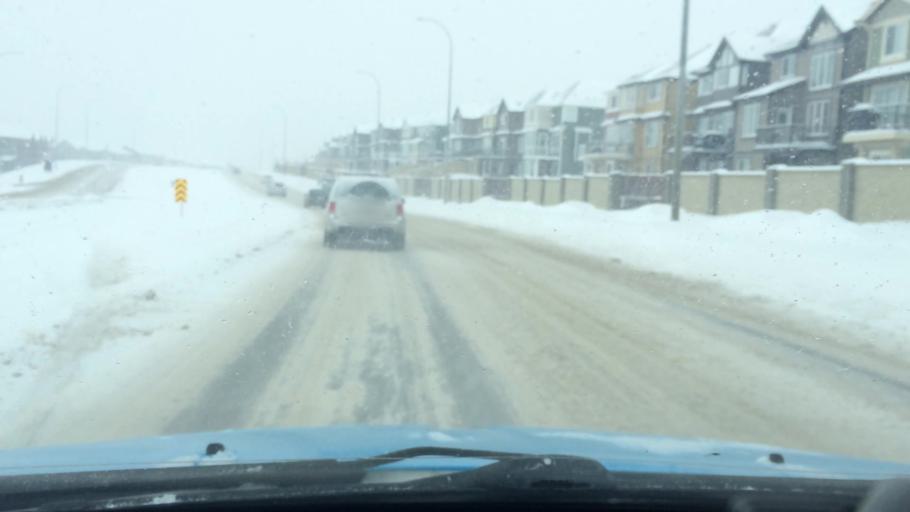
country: CA
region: Alberta
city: Calgary
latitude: 51.1659
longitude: -114.1499
